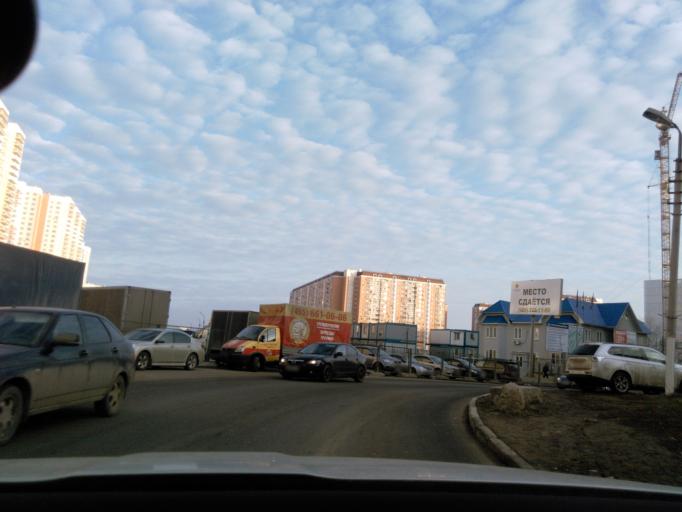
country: RU
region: Moscow
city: Khimki
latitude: 55.9031
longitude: 37.4029
